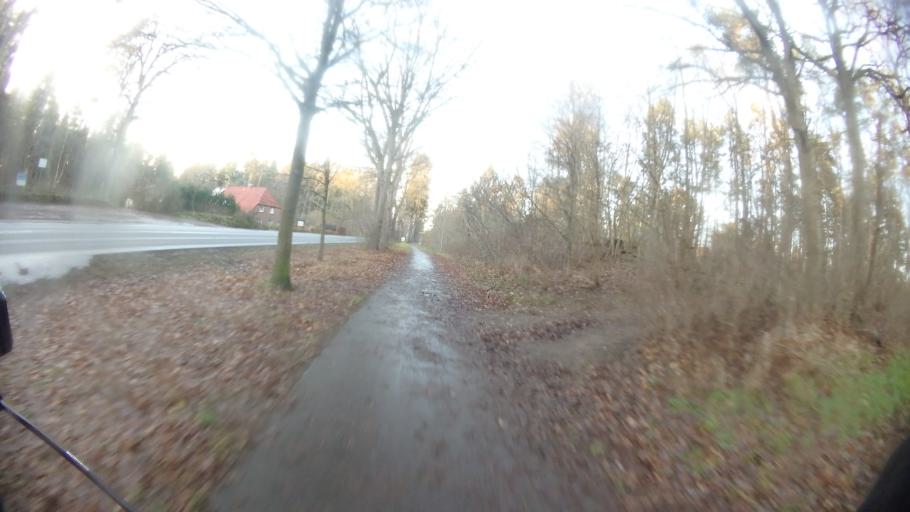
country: DE
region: Schleswig-Holstein
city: Ratekau
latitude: 53.9933
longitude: 10.7089
